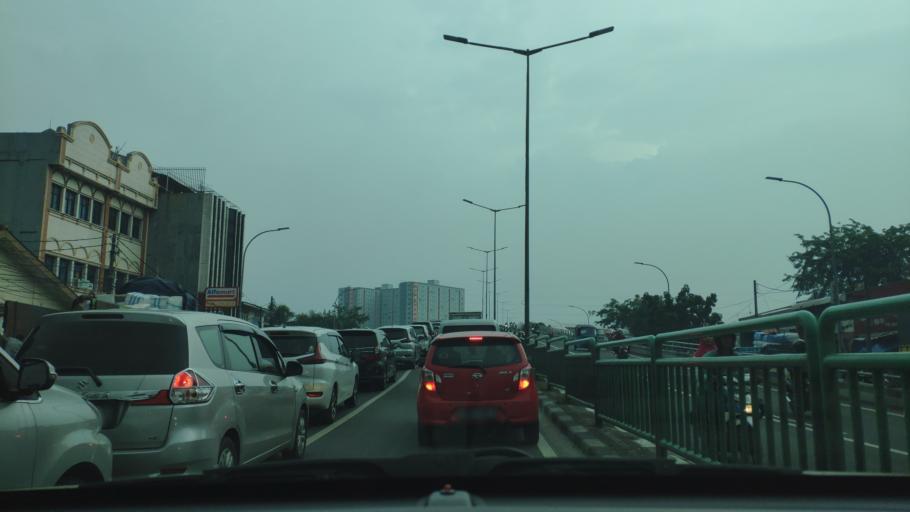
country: ID
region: Jakarta Raya
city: Jakarta
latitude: -6.1833
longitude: 106.8126
